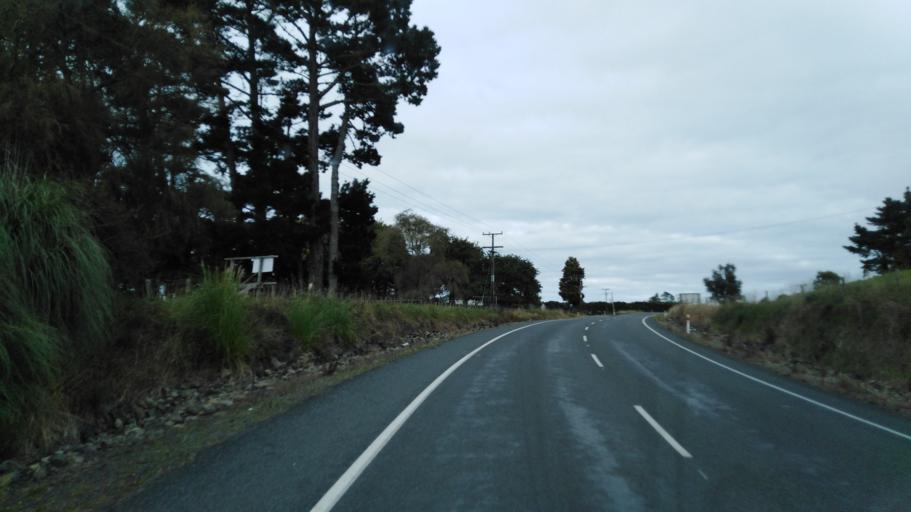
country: NZ
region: Bay of Plenty
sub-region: Western Bay of Plenty District
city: Waihi Beach
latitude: -37.4156
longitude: 175.9090
